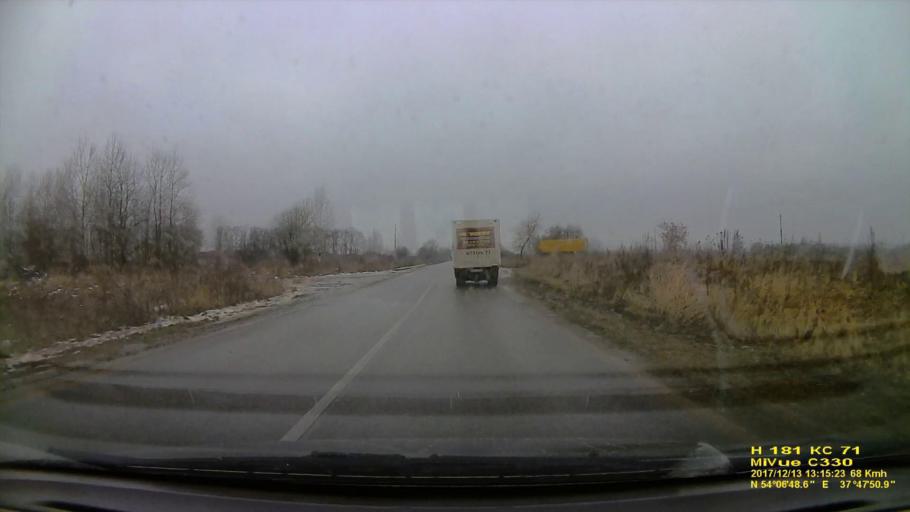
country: RU
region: Tula
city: Bolokhovo
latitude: 54.1135
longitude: 37.7973
